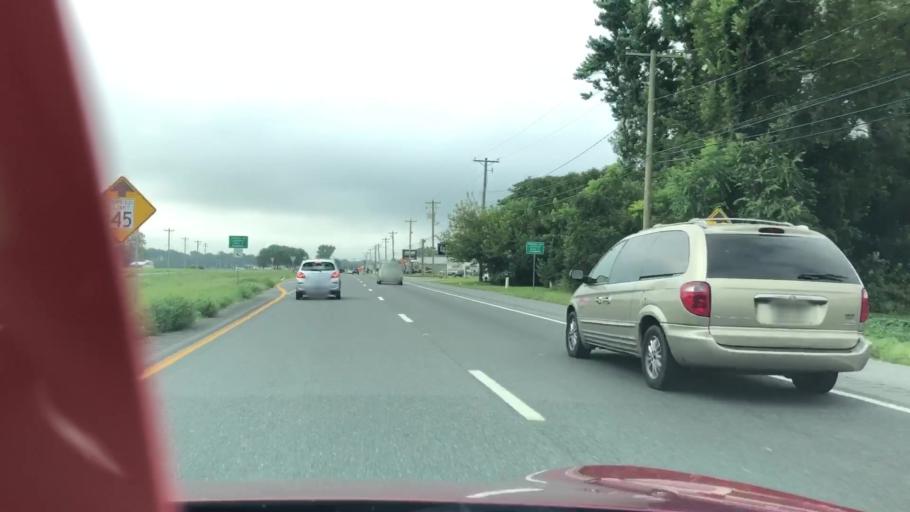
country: US
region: Delaware
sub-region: Sussex County
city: Bridgeville
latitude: 38.8134
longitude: -75.5854
